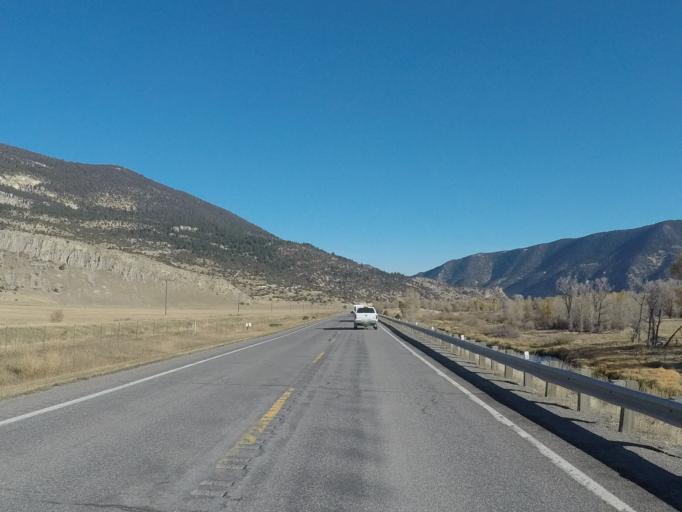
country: US
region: Montana
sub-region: Park County
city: Livingston
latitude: 45.5670
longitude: -110.5907
